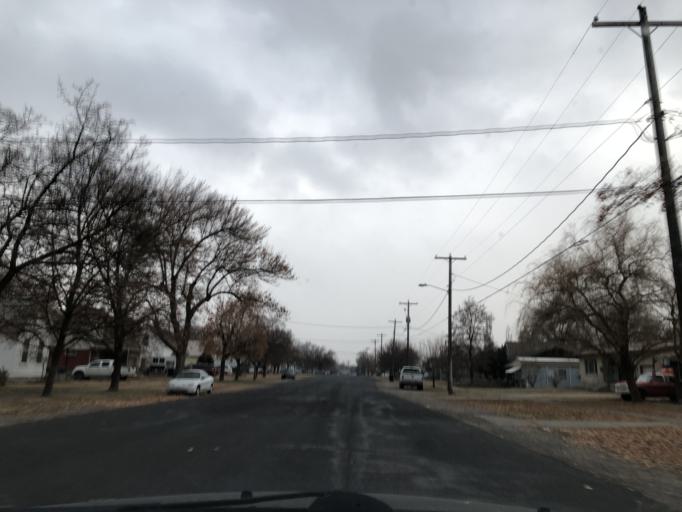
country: US
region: Utah
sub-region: Cache County
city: Logan
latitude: 41.7313
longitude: -111.8479
